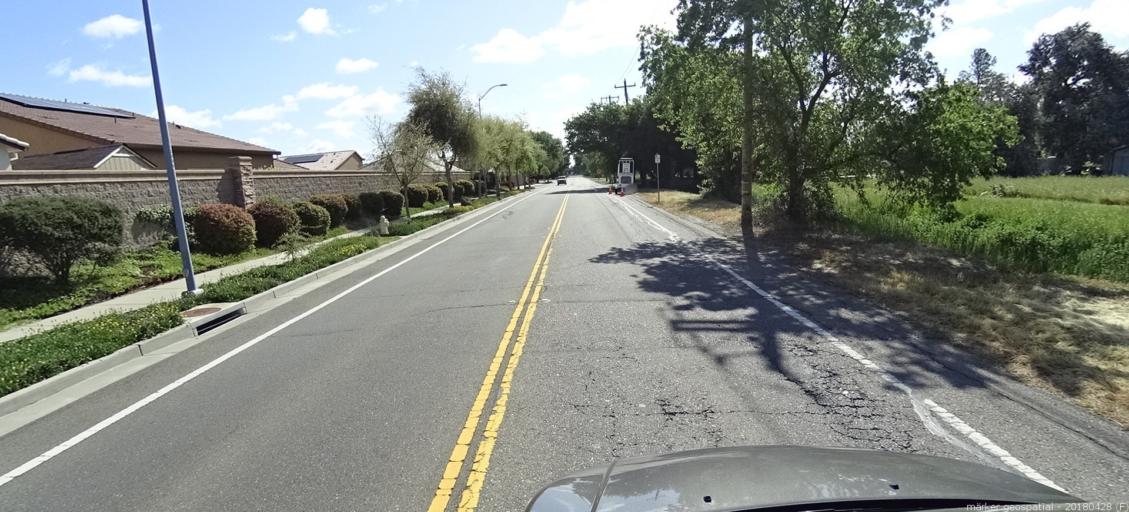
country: US
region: California
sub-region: Yolo County
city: West Sacramento
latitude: 38.5351
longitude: -121.5589
